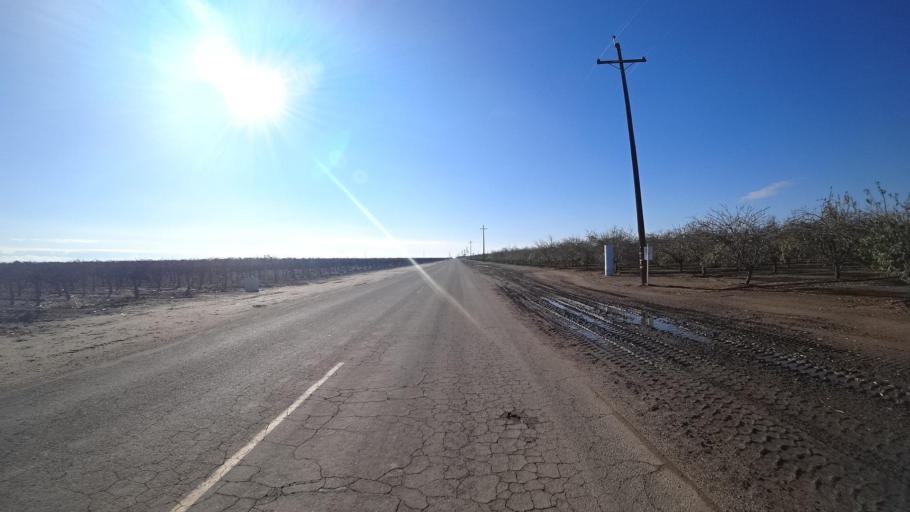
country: US
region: California
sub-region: Kern County
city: Delano
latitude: 35.7217
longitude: -119.2764
